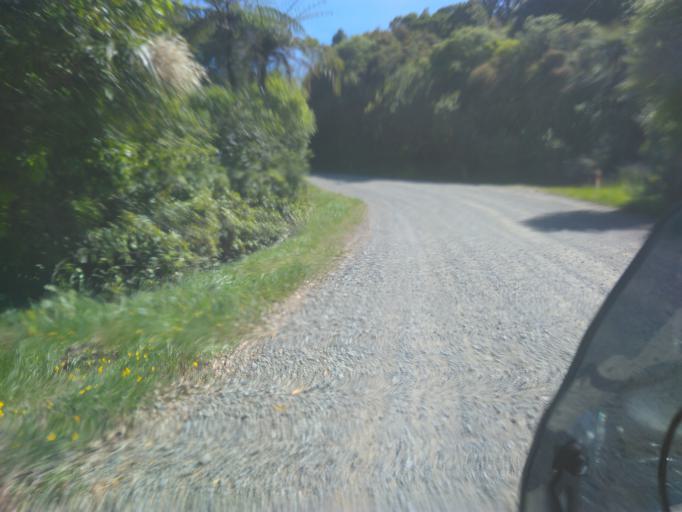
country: NZ
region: Hawke's Bay
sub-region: Wairoa District
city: Wairoa
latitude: -38.7956
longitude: 177.1248
